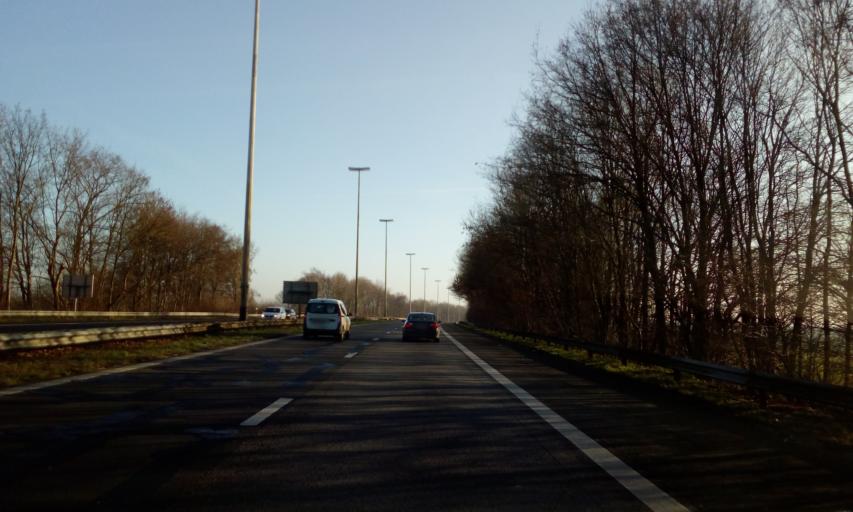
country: BE
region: Wallonia
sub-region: Province du Brabant Wallon
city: Nivelles
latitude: 50.5600
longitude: 4.3534
